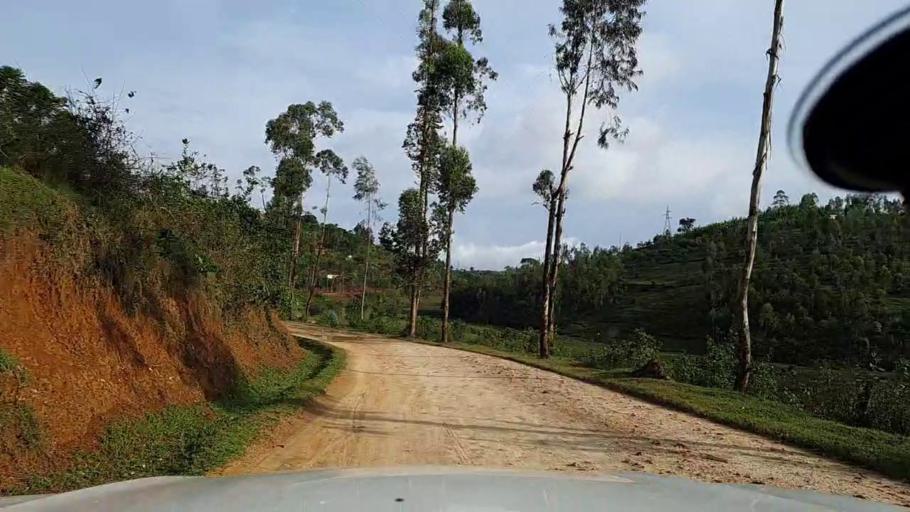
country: RW
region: Southern Province
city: Gitarama
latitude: -2.1748
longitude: 29.5558
